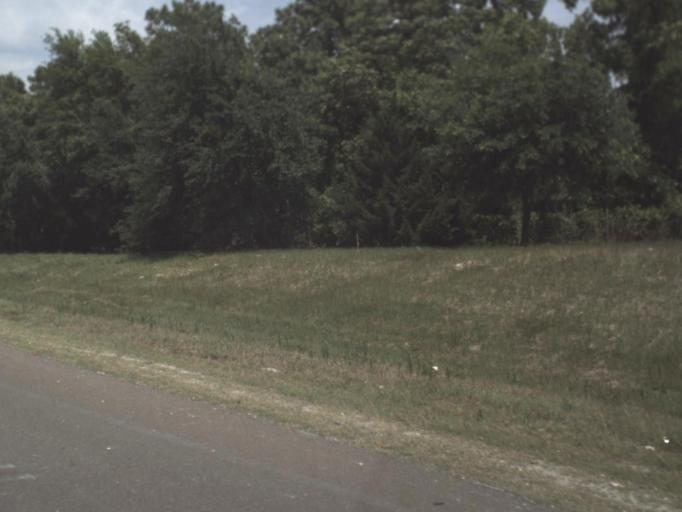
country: US
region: Florida
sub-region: Duval County
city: Jacksonville
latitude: 30.4251
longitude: -81.5707
